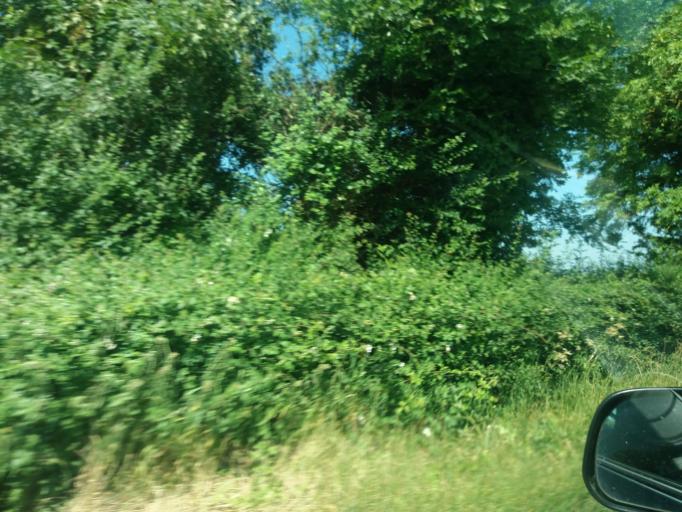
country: IE
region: Leinster
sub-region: An Mhi
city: Stamullin
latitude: 53.5853
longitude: -6.2992
